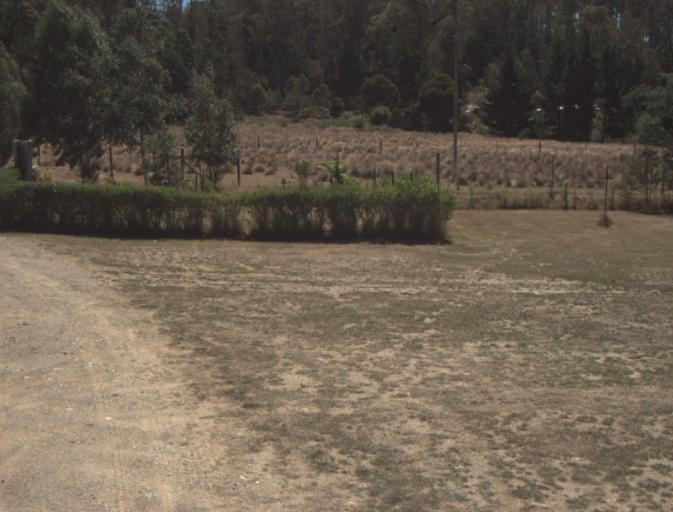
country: AU
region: Tasmania
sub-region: Dorset
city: Scottsdale
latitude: -41.3000
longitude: 147.3787
